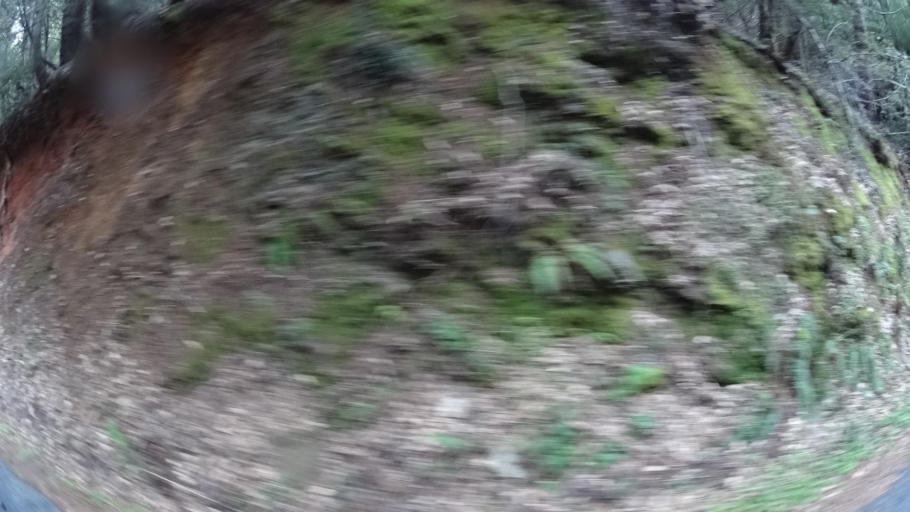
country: US
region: California
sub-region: Humboldt County
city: Willow Creek
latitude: 41.2003
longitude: -123.7824
